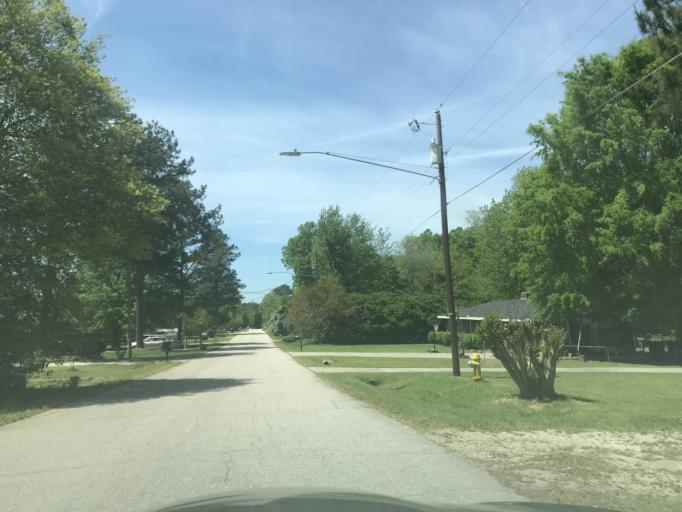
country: US
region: North Carolina
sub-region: Wake County
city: Raleigh
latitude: 35.8257
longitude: -78.5717
